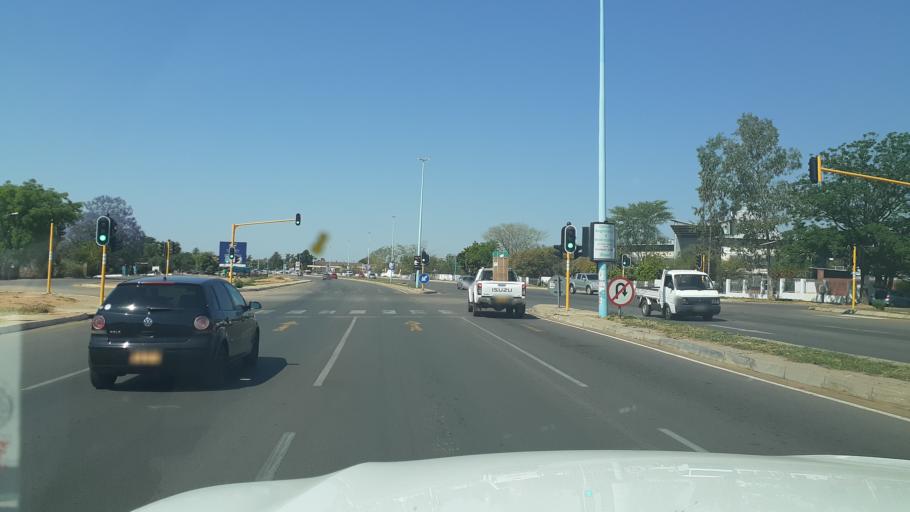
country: BW
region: South East
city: Gaborone
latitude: -24.6797
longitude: 25.9165
